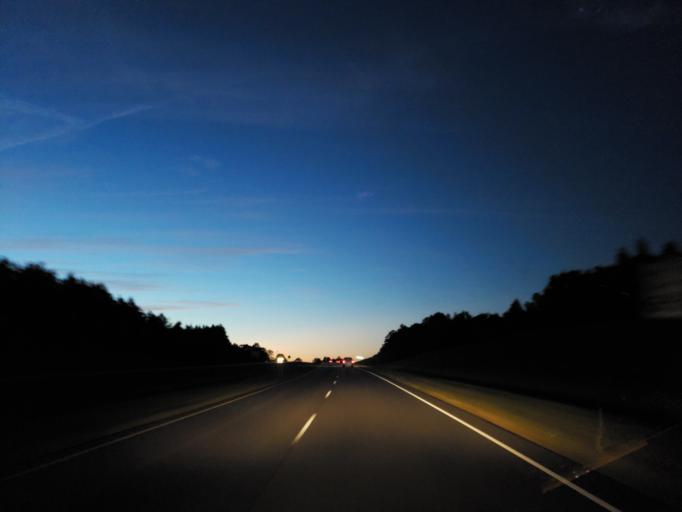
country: US
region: Mississippi
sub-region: Clarke County
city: Quitman
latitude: 32.1038
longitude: -88.7088
